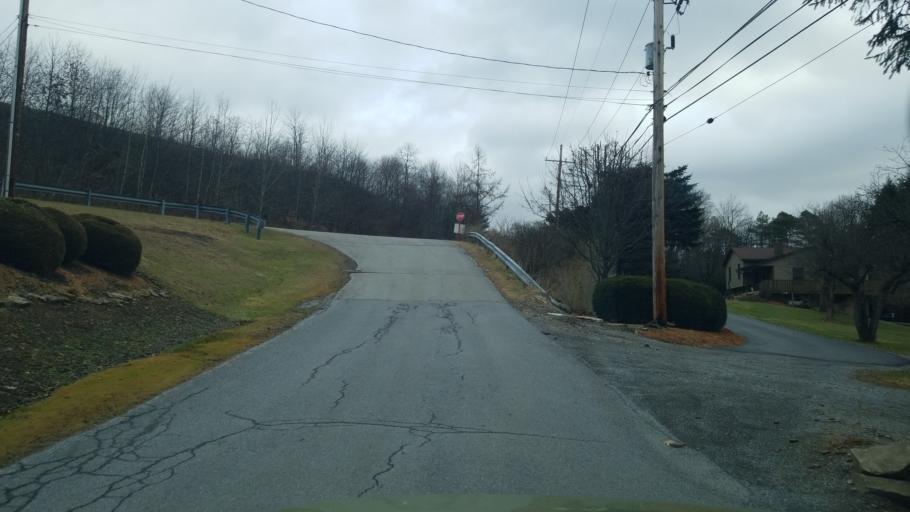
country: US
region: Pennsylvania
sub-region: Clearfield County
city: Clearfield
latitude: 41.0287
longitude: -78.4045
